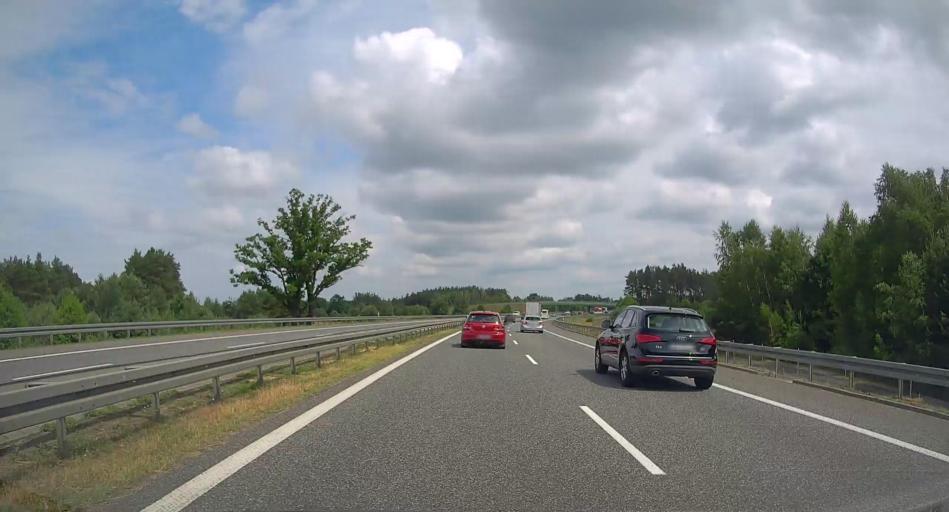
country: PL
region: Masovian Voivodeship
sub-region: Powiat wyszkowski
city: Wyszkow
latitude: 52.5490
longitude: 21.4391
